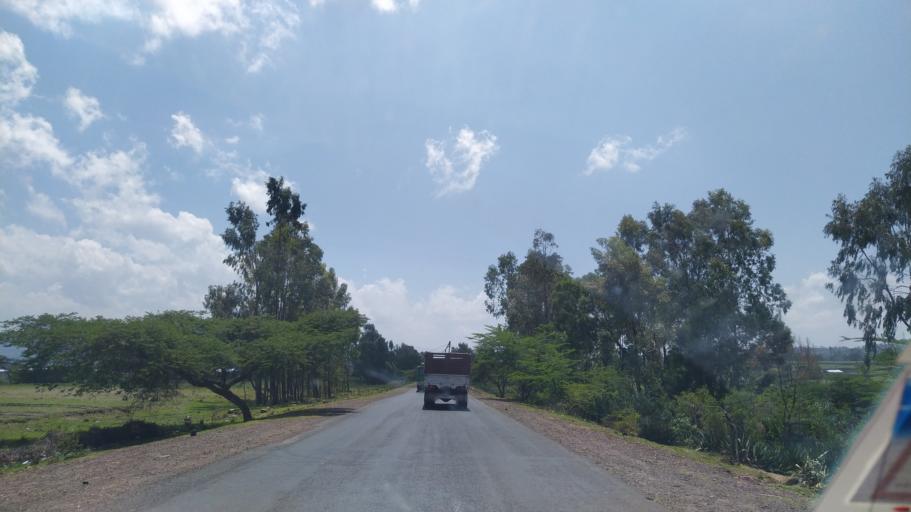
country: ET
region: Southern Nations, Nationalities, and People's Region
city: Butajira
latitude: 7.7662
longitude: 38.1360
